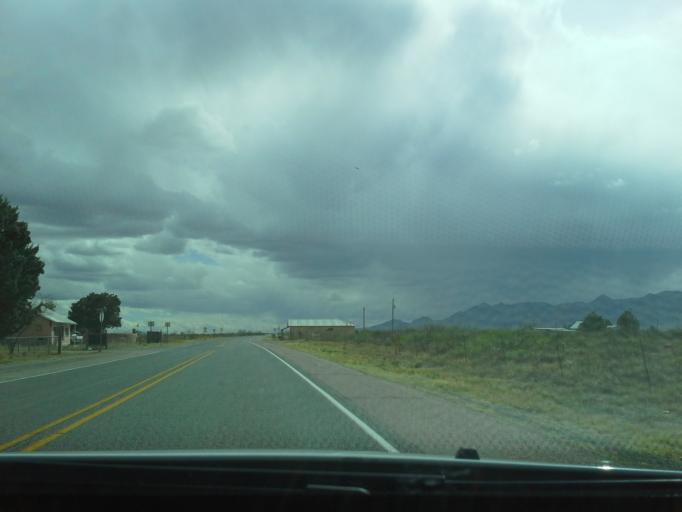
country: US
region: New Mexico
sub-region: Hidalgo County
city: Lordsburg
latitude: 31.8347
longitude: -109.0324
